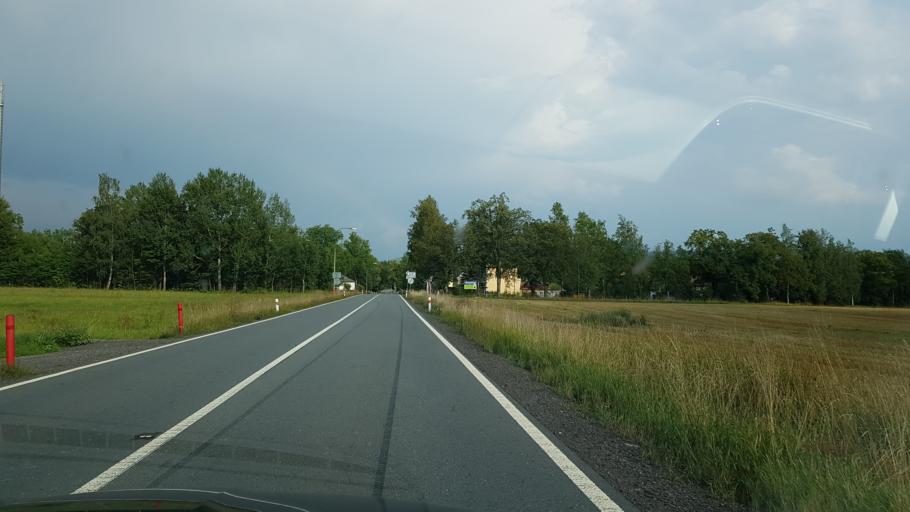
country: CZ
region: Pardubicky
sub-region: Okres Usti nad Orlici
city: Kraliky
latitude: 50.0894
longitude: 16.7166
